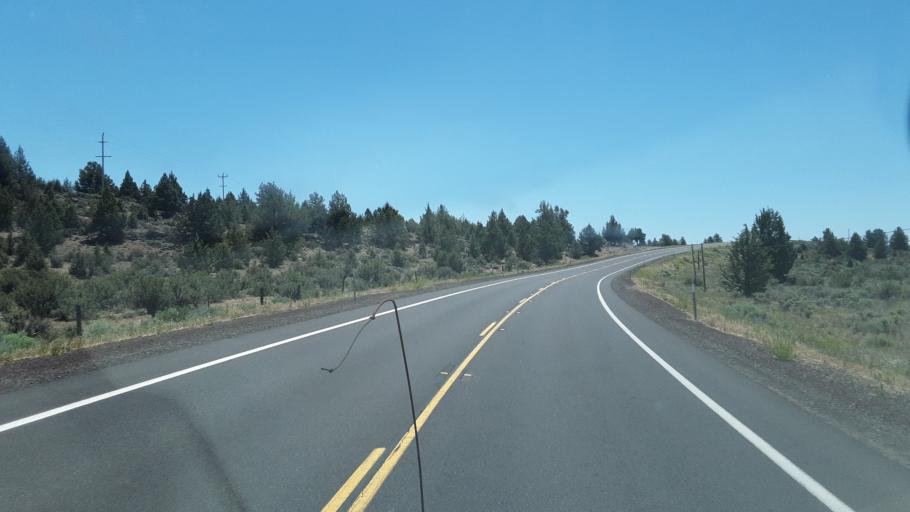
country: US
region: California
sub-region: Siskiyou County
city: Tulelake
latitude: 41.7097
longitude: -121.2824
